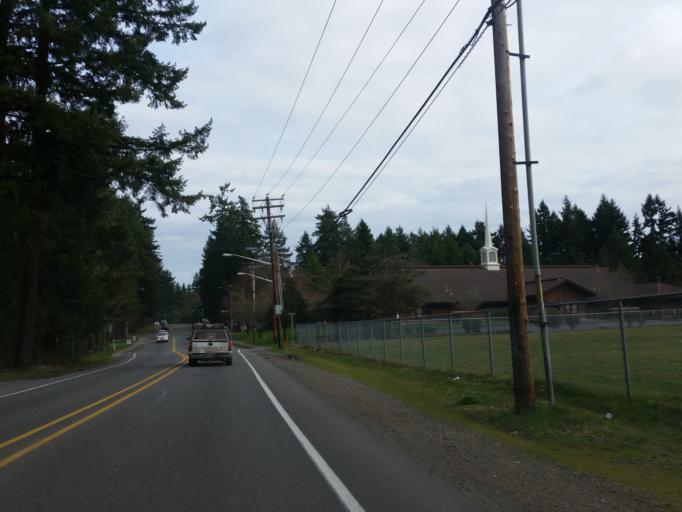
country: US
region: Washington
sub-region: Pierce County
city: South Hill
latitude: 47.1429
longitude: -122.2608
